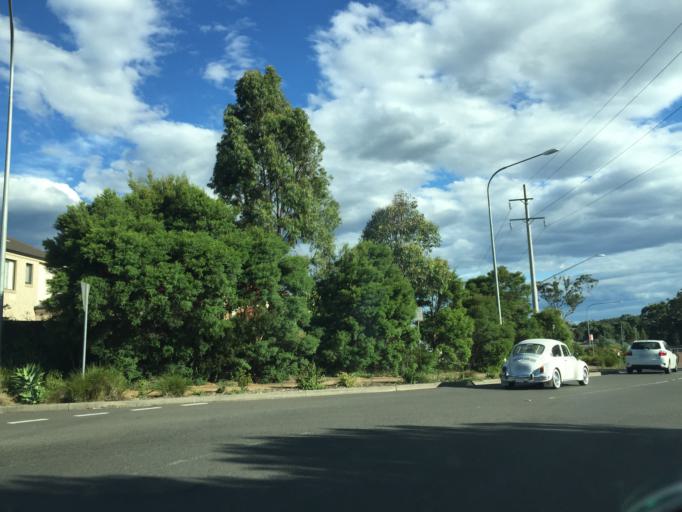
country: AU
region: New South Wales
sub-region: The Hills Shire
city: Glenhaven
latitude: -33.7094
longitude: 150.9741
